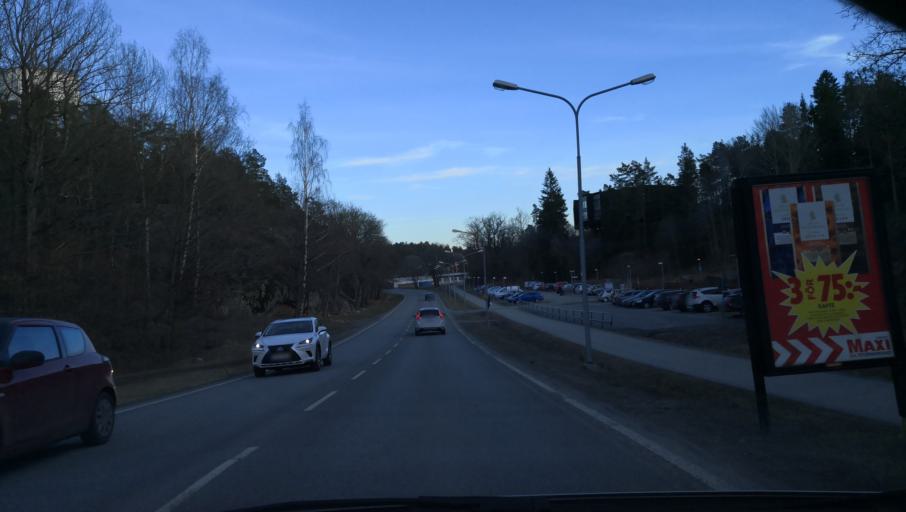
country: SE
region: Stockholm
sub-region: Varmdo Kommun
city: Gustavsberg
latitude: 59.3317
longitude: 18.3891
